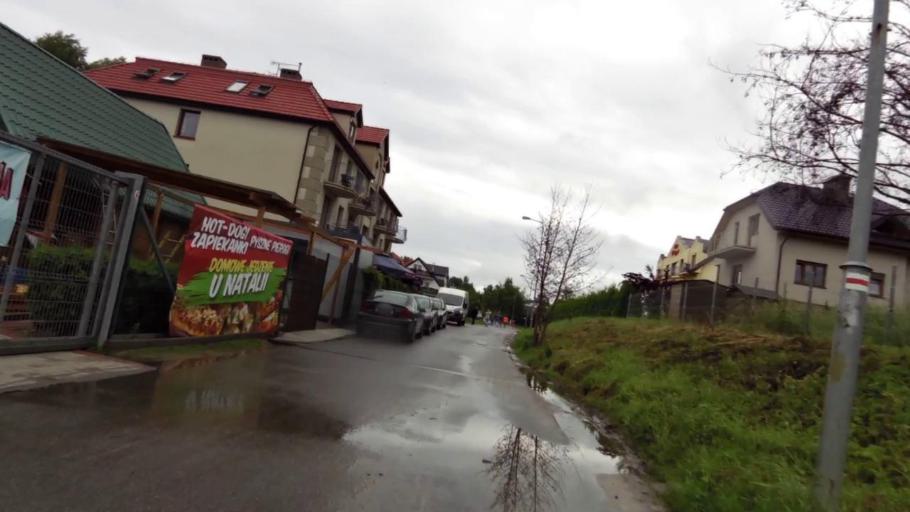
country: PL
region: West Pomeranian Voivodeship
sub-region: Powiat koszalinski
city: Mielno
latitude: 54.2471
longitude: 15.9367
